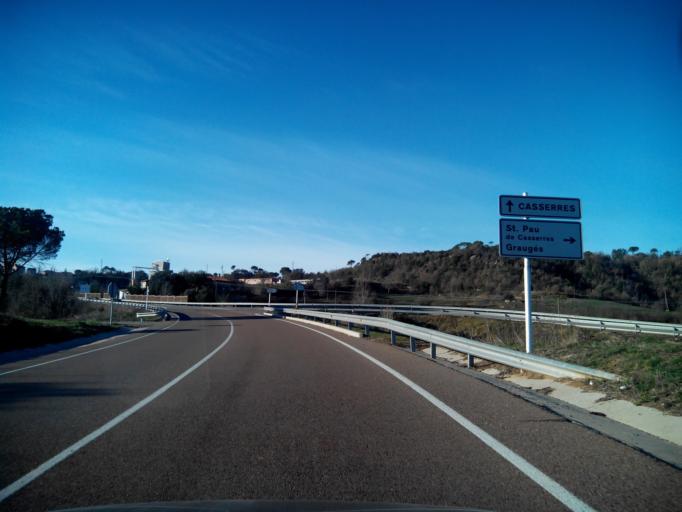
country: ES
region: Catalonia
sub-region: Provincia de Barcelona
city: Gironella
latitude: 42.0200
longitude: 1.8413
